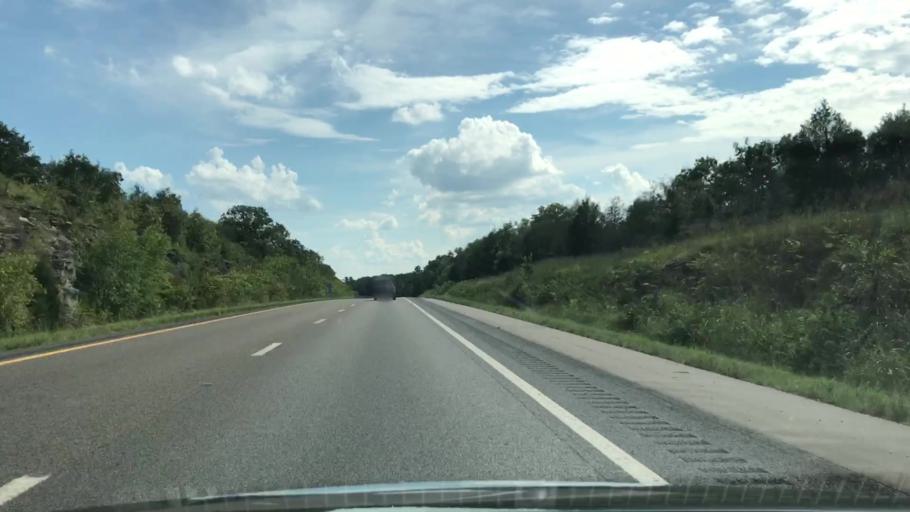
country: US
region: Tennessee
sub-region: Maury County
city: Columbia
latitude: 35.5603
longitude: -86.9072
